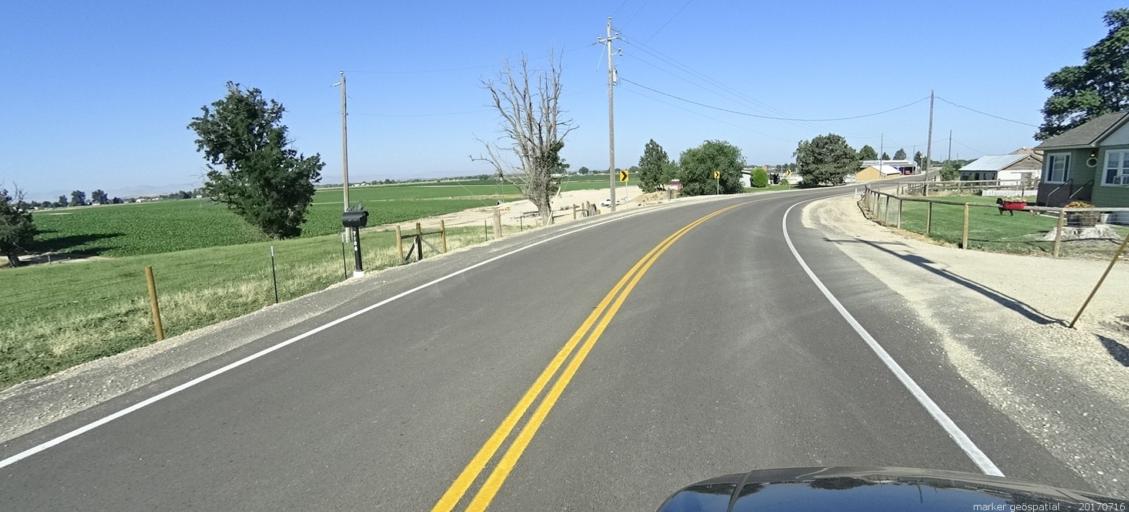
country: US
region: Idaho
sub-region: Canyon County
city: Nampa
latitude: 43.5467
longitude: -116.4831
